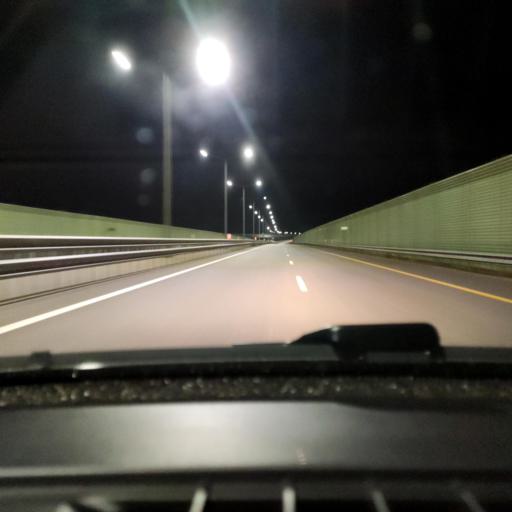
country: RU
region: Voronezj
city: Novaya Usman'
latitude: 51.6042
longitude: 39.3325
